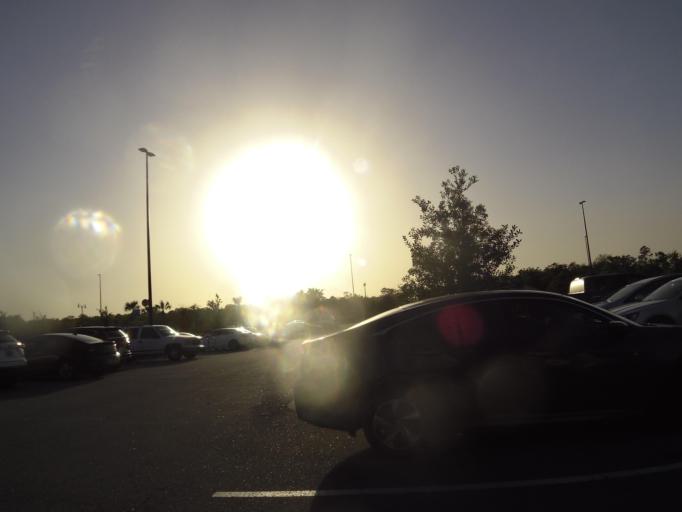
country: US
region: Florida
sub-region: Saint Johns County
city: Fruit Cove
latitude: 30.0946
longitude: -81.5215
